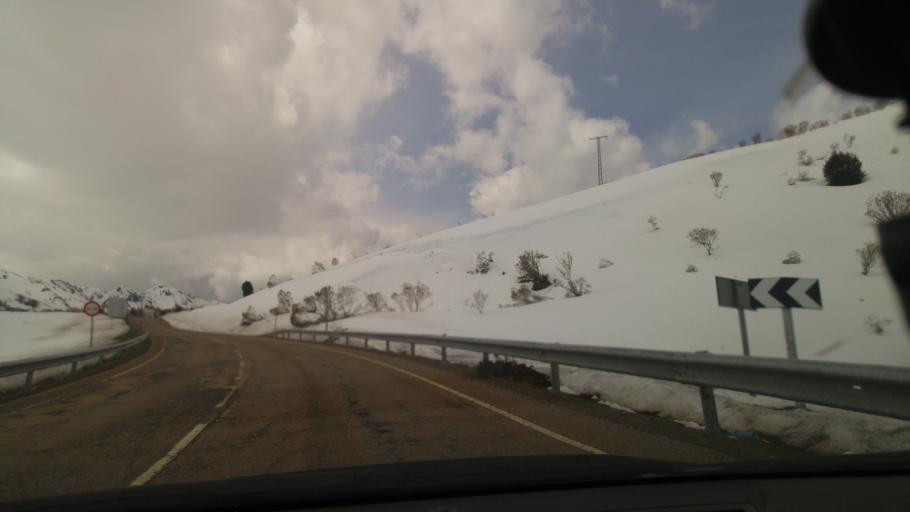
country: ES
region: Asturias
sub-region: Province of Asturias
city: Campo de Caso
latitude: 43.0660
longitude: -5.3827
